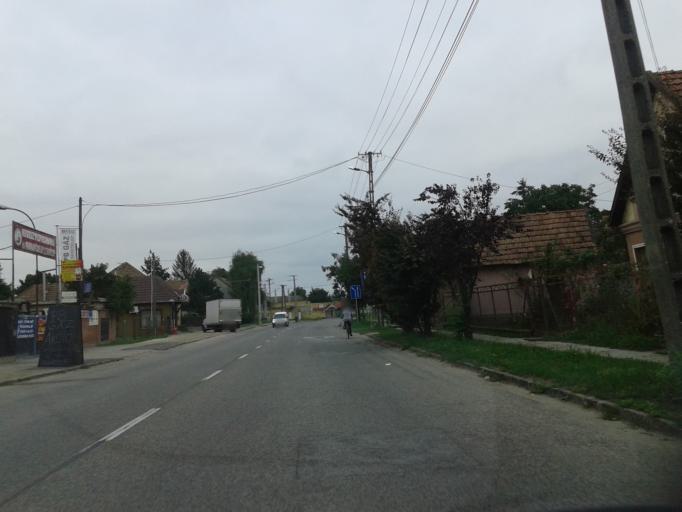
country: HU
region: Pest
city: Domsod
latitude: 47.0958
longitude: 19.0087
